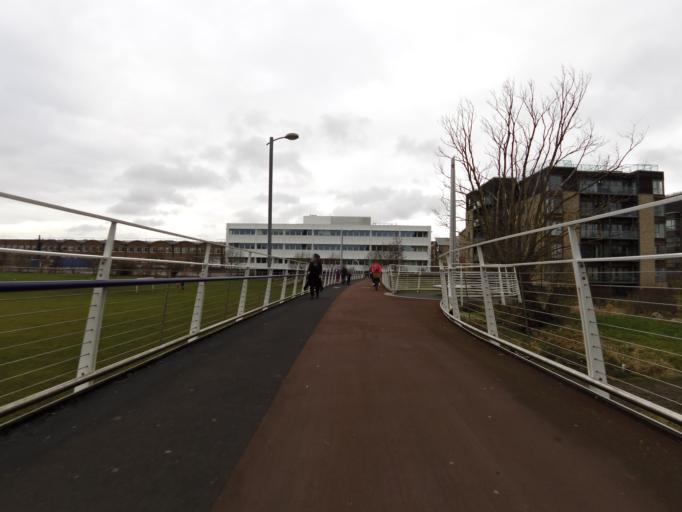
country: GB
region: England
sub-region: Cambridgeshire
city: Cambridge
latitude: 52.2140
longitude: 0.1422
